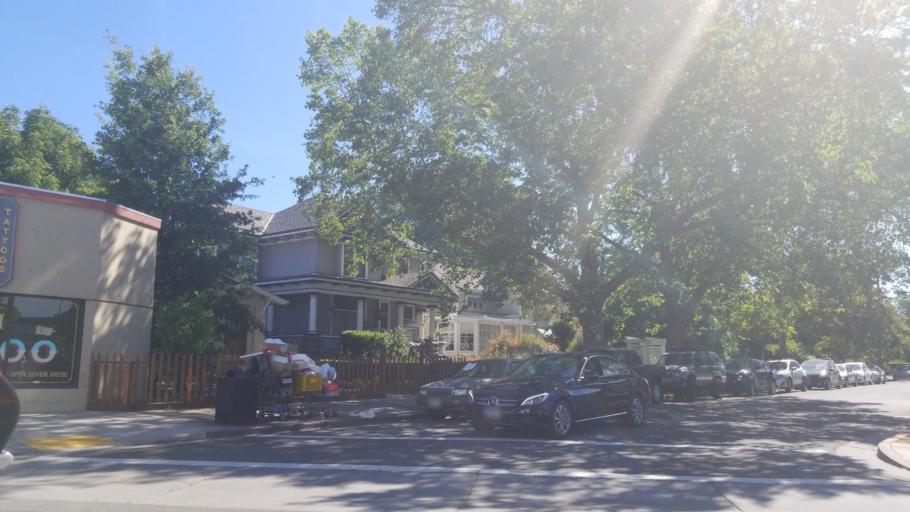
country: US
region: California
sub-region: Sonoma County
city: Santa Rosa
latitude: 38.4446
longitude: -122.7170
